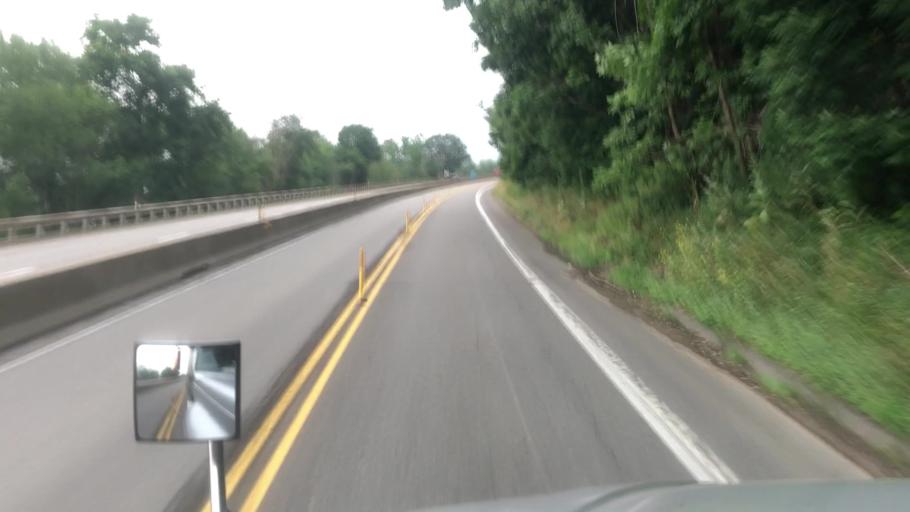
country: US
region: Pennsylvania
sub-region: Venango County
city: Woodland Heights
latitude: 41.4134
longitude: -79.7333
